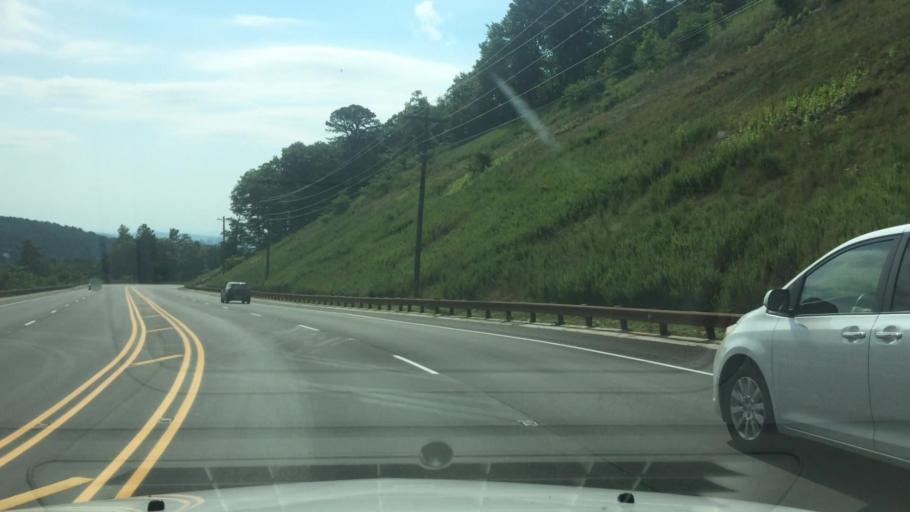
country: US
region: North Carolina
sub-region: Watauga County
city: Blowing Rock
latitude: 36.1071
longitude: -81.6537
